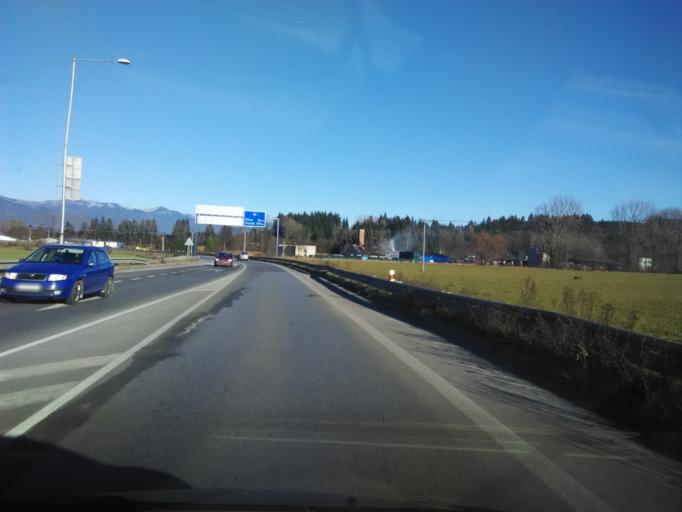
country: SK
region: Zilinsky
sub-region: Okres Martin
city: Martin
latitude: 49.0384
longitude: 18.9100
